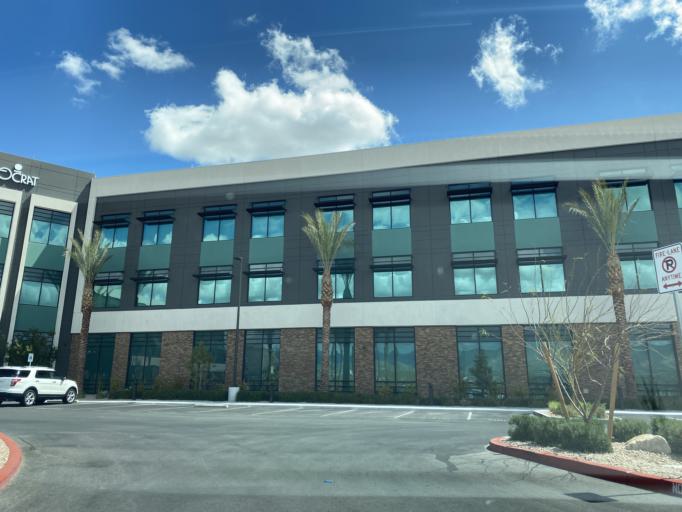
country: US
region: Nevada
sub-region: Clark County
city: Summerlin South
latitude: 36.1168
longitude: -115.3165
